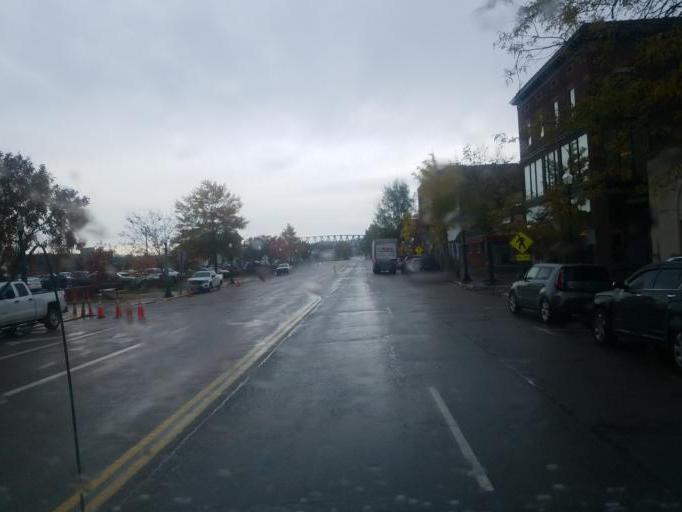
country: US
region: Ohio
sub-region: Washington County
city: Marietta
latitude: 39.4151
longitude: -81.4544
